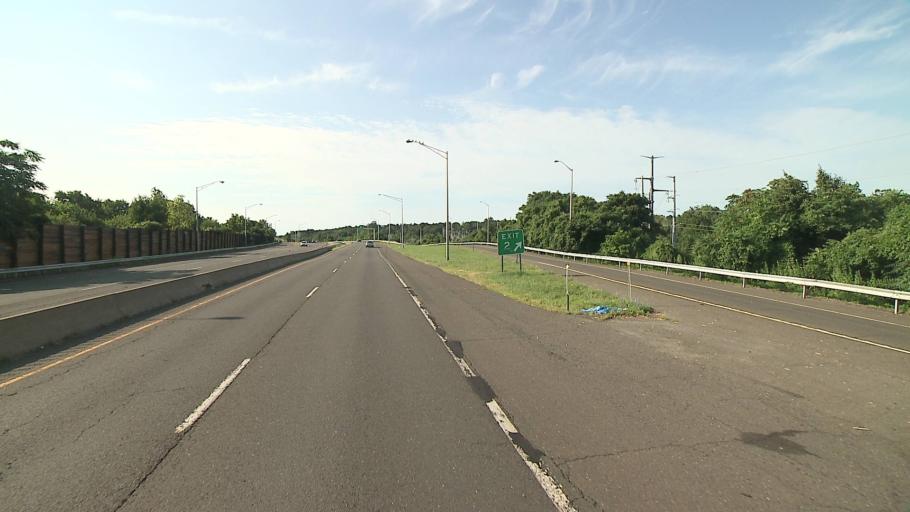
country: US
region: Connecticut
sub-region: Fairfield County
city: Norwalk
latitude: 41.1312
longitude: -73.4286
